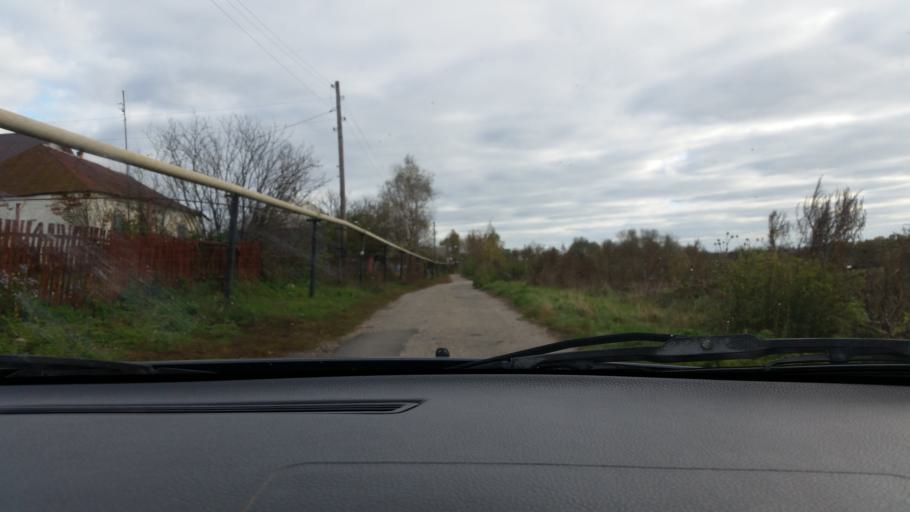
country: RU
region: Lipetsk
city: Gryazi
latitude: 52.4532
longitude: 39.9817
